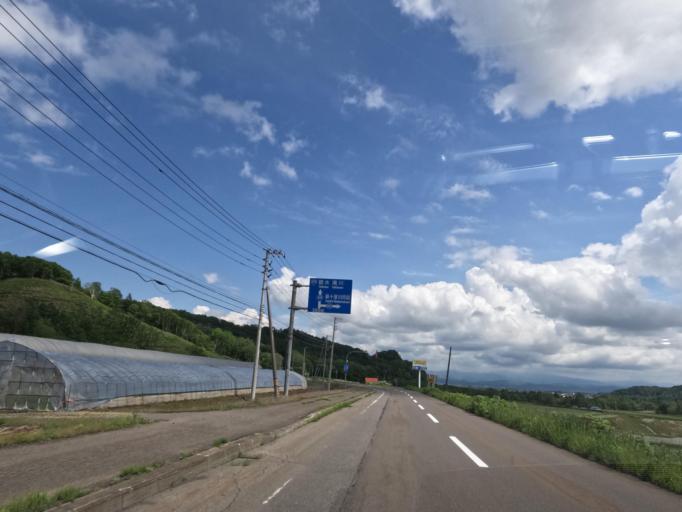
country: JP
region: Hokkaido
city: Takikawa
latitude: 43.5797
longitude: 141.8265
